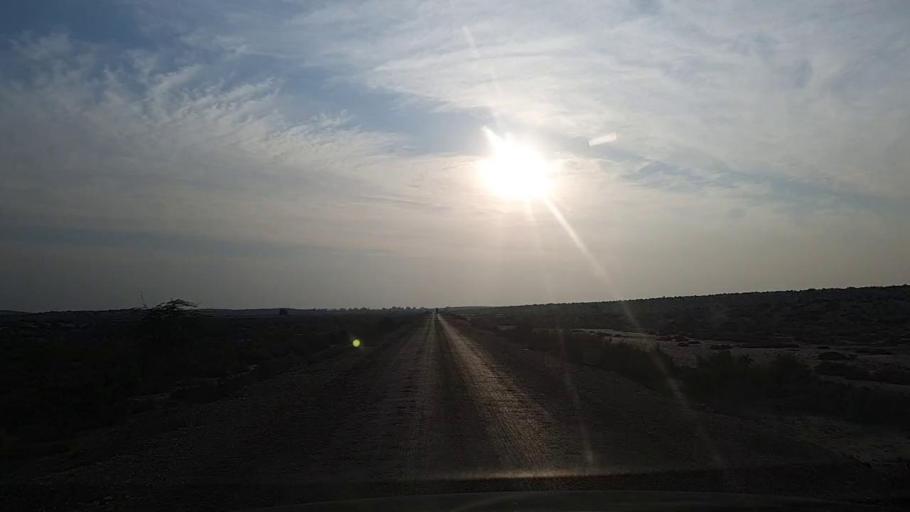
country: PK
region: Sindh
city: Jam Sahib
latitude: 26.4172
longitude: 68.5195
